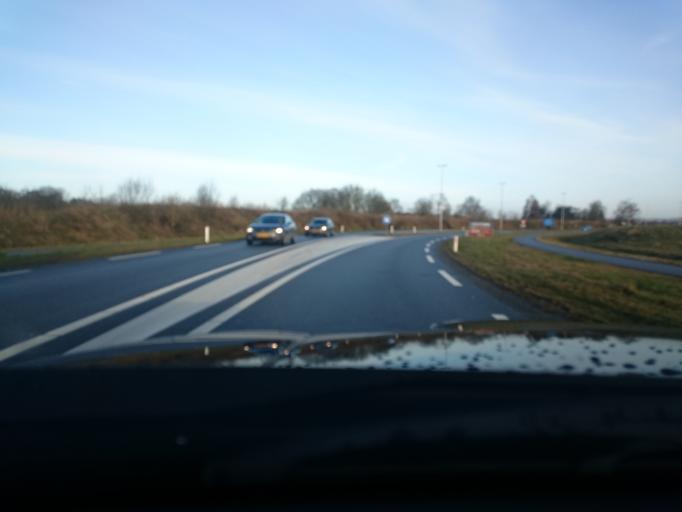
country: NL
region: Overijssel
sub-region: Gemeente Deventer
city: Schalkhaar
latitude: 52.3200
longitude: 6.2022
